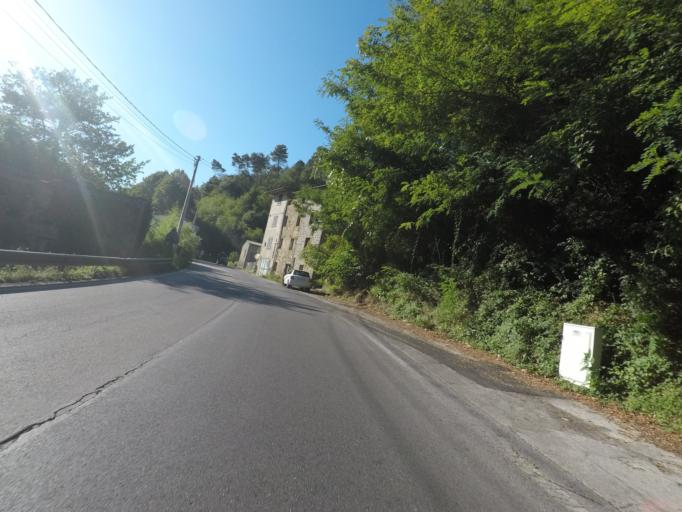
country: IT
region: Tuscany
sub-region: Provincia di Lucca
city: Massarosa
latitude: 43.9033
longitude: 10.3745
